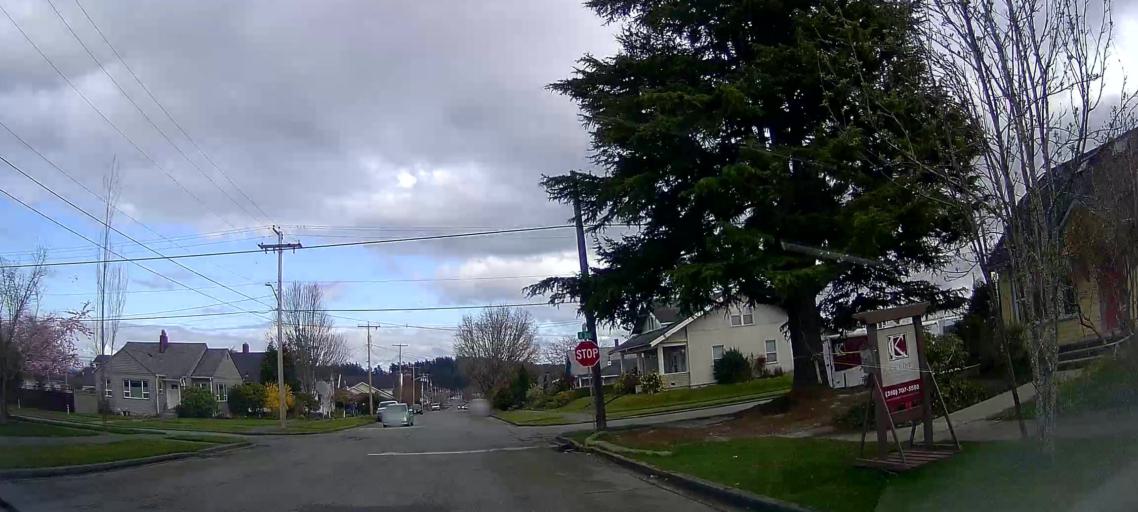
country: US
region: Washington
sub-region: Skagit County
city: Anacortes
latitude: 48.5151
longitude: -122.6208
